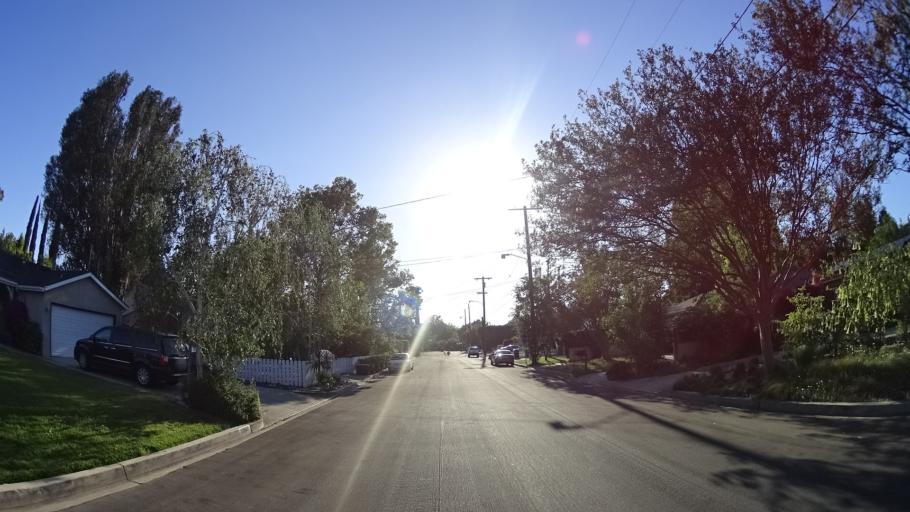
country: US
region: California
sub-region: Los Angeles County
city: North Hollywood
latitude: 34.1639
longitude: -118.4023
